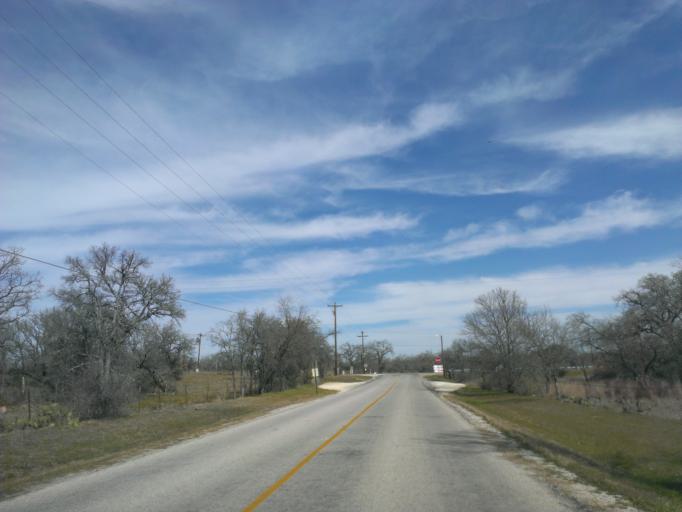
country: US
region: Texas
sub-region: Burnet County
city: Granite Shoals
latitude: 30.6164
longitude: -98.3916
